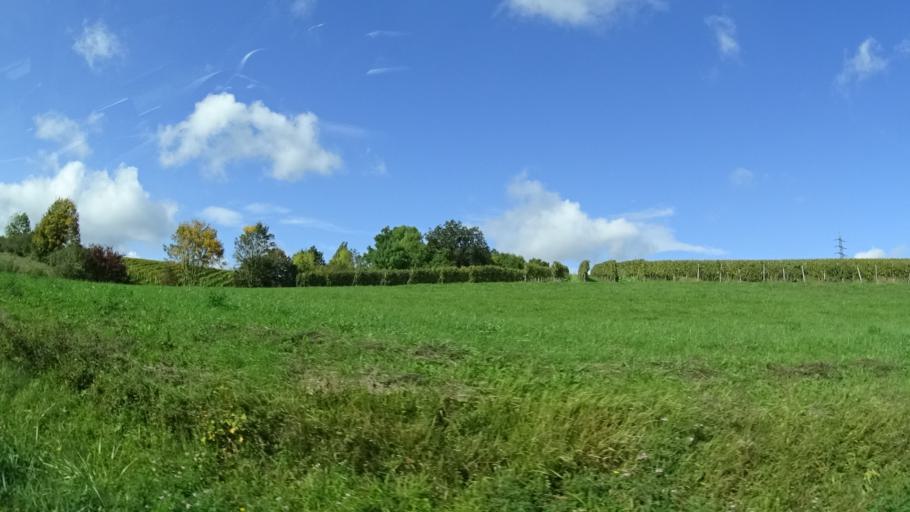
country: DE
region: Bavaria
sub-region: Regierungsbezirk Unterfranken
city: Buchbrunn
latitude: 49.7358
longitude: 10.1137
